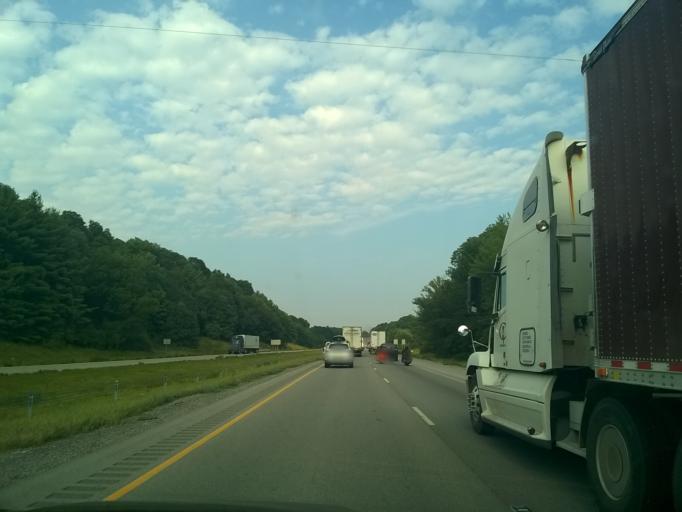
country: US
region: Indiana
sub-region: Putnam County
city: Cloverdale
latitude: 39.5297
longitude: -86.8662
